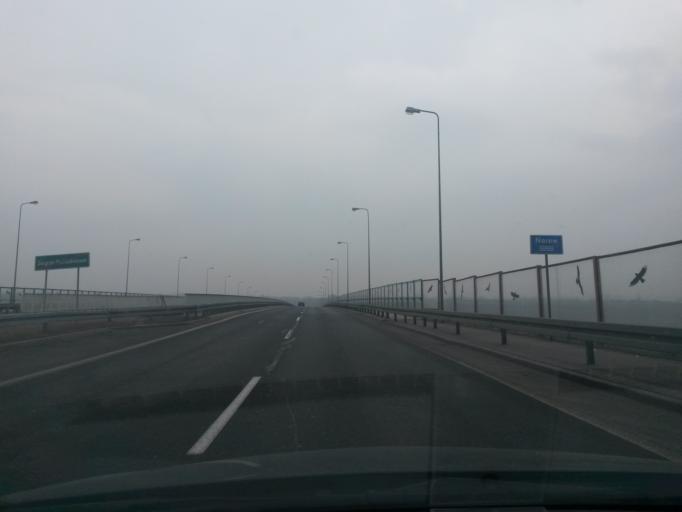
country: PL
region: Masovian Voivodeship
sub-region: Powiat legionowski
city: Nieporet
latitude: 52.4556
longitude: 21.0163
